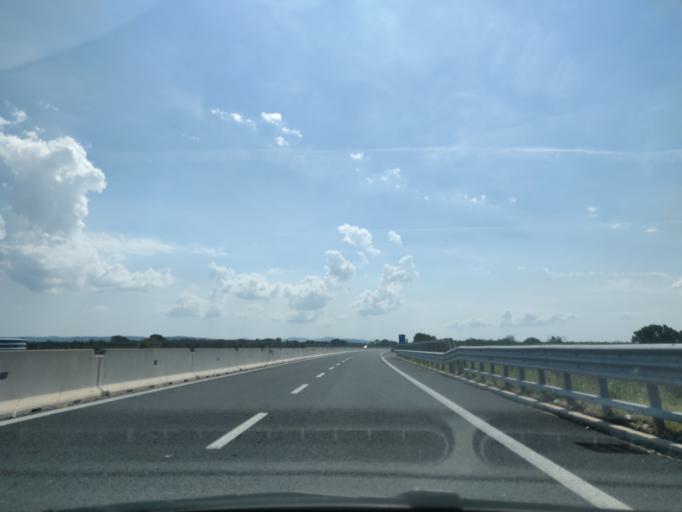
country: IT
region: Latium
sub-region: Provincia di Viterbo
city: Blera
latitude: 42.3231
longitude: 11.9892
